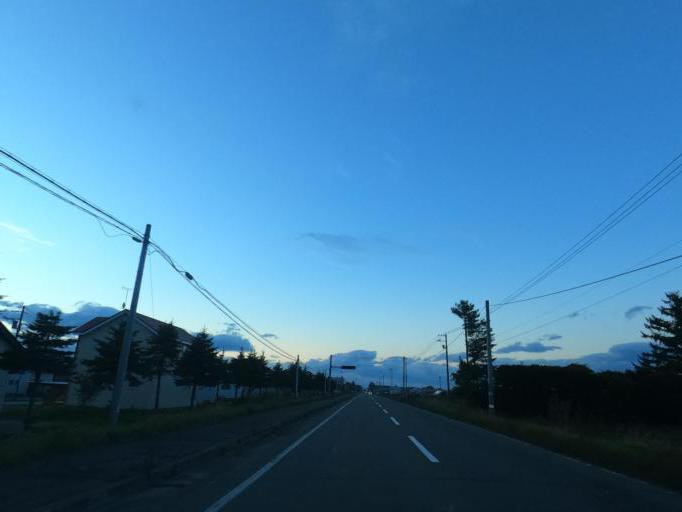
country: JP
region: Hokkaido
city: Obihiro
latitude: 42.6474
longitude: 143.1963
